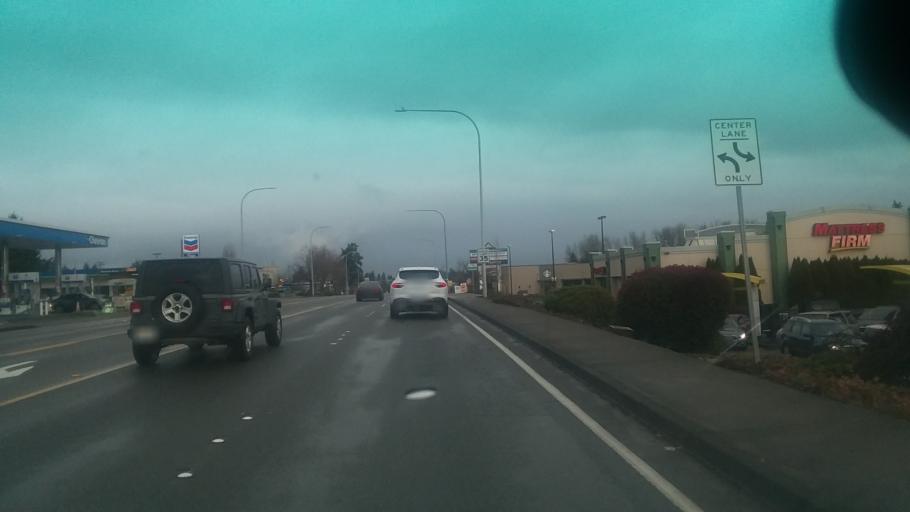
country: US
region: Washington
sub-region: Pierce County
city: South Hill
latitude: 47.1484
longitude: -122.2929
